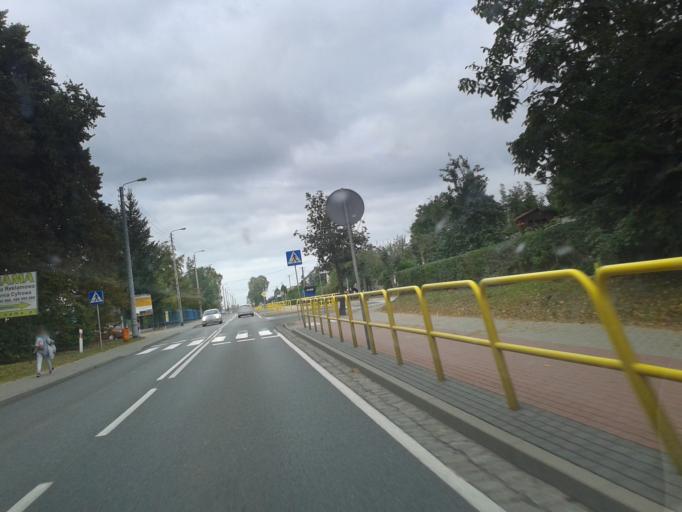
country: PL
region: Kujawsko-Pomorskie
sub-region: Powiat sepolenski
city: Sepolno Krajenskie
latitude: 53.4603
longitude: 17.5317
